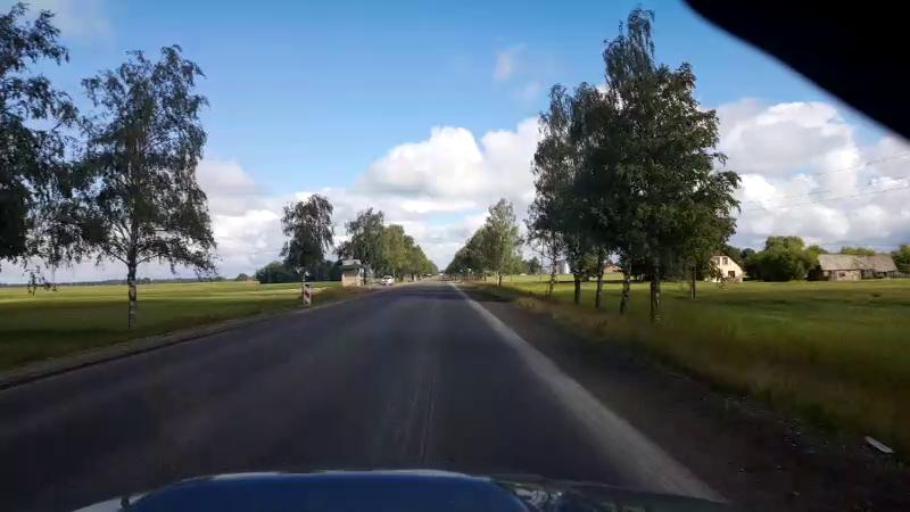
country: LV
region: Bauskas Rajons
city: Bauska
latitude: 56.3482
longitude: 24.2888
